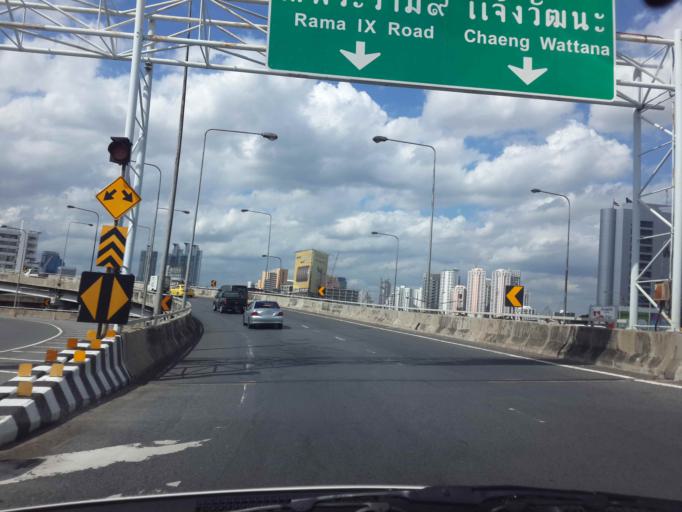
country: TH
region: Bangkok
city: Khlong Toei
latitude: 13.7151
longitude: 100.5554
